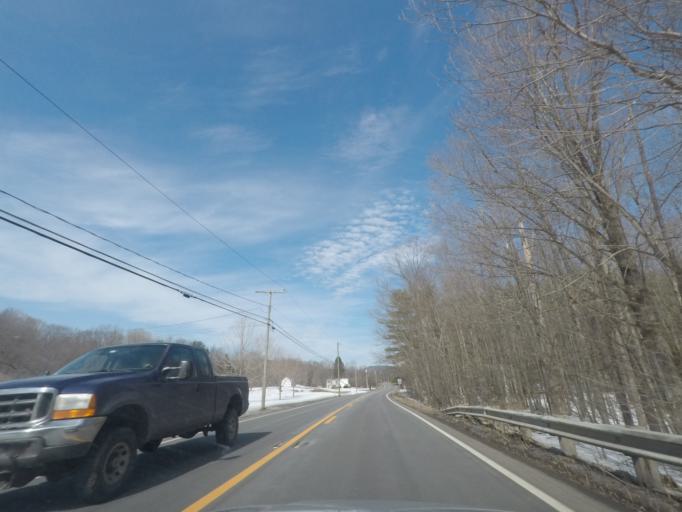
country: US
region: Massachusetts
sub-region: Berkshire County
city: West Stockbridge
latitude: 42.3583
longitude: -73.3810
